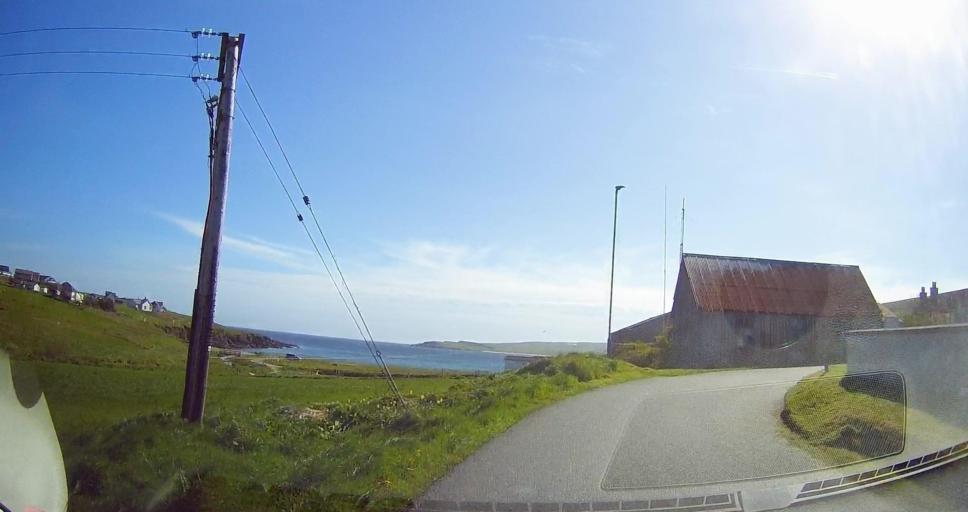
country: GB
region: Scotland
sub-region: Shetland Islands
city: Sandwick
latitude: 59.9986
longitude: -1.2538
